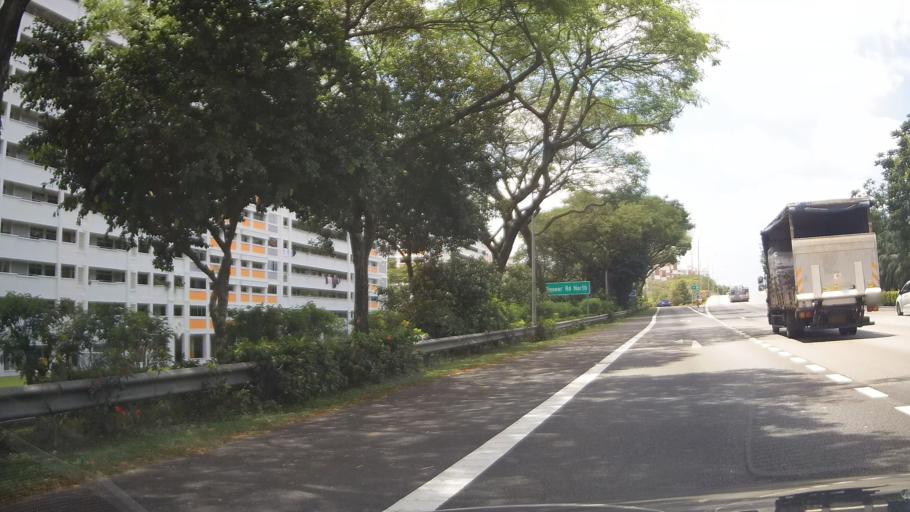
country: MY
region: Johor
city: Johor Bahru
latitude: 1.3481
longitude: 103.6929
